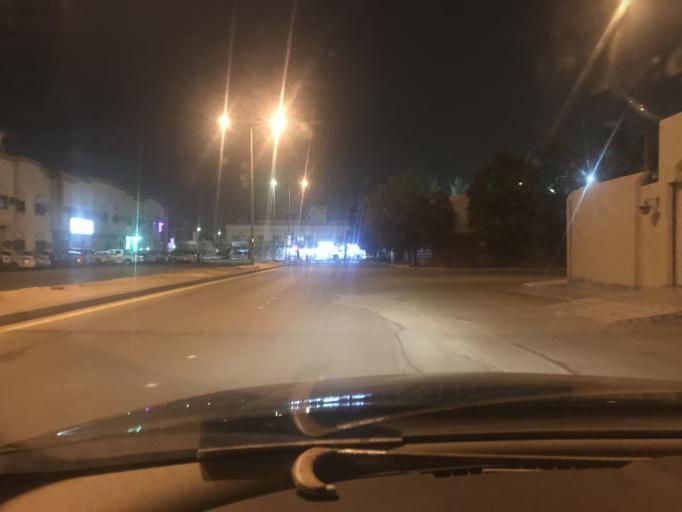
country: SA
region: Ar Riyad
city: Riyadh
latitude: 24.7510
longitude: 46.7788
